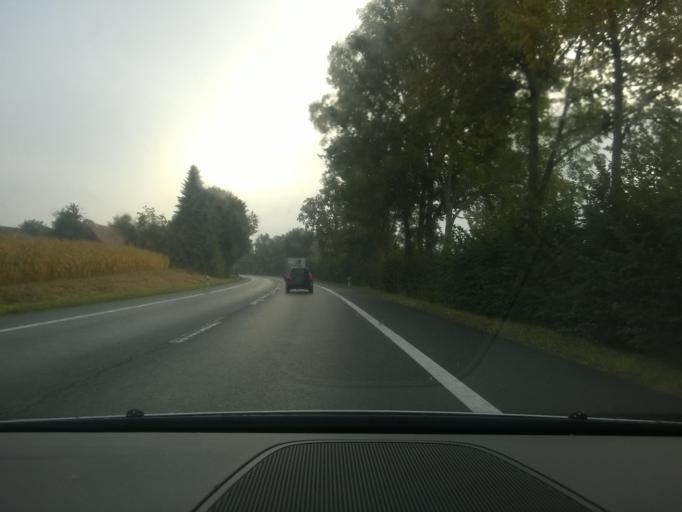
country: DE
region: North Rhine-Westphalia
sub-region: Regierungsbezirk Munster
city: Coesfeld
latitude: 51.9288
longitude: 7.1896
